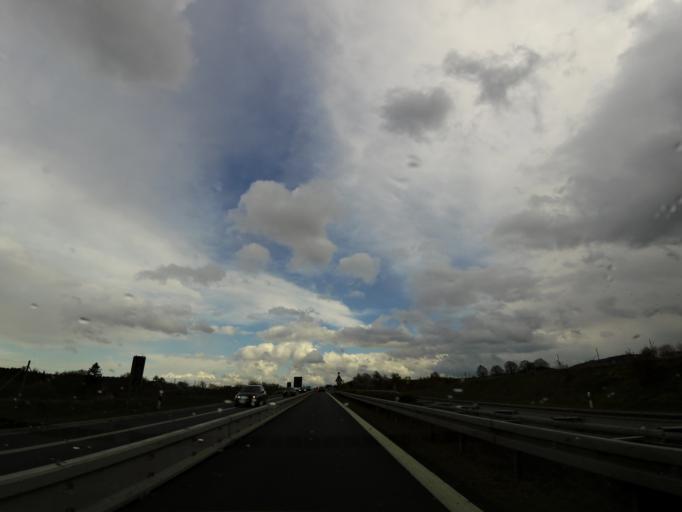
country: DE
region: Saxony-Anhalt
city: Blankenburg
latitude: 51.8210
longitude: 10.9283
